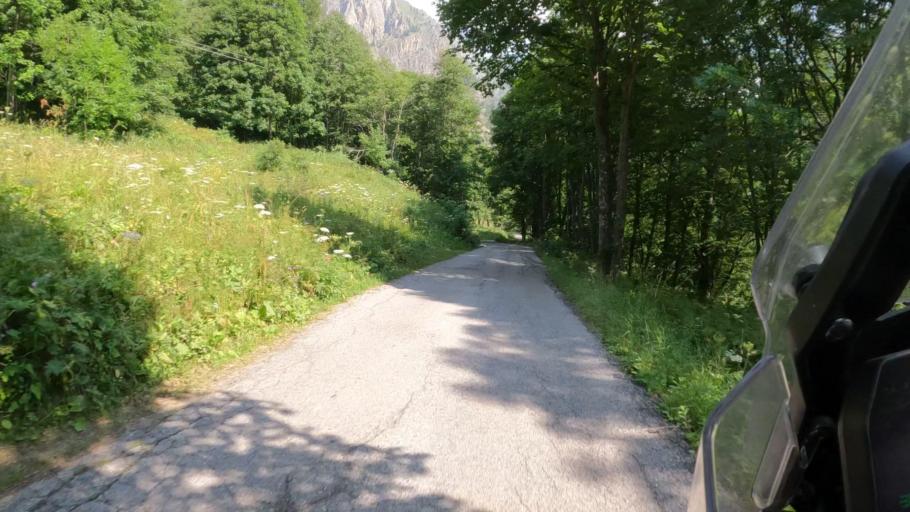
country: IT
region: Piedmont
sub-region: Provincia di Cuneo
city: Canosio
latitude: 44.4300
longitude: 7.0538
